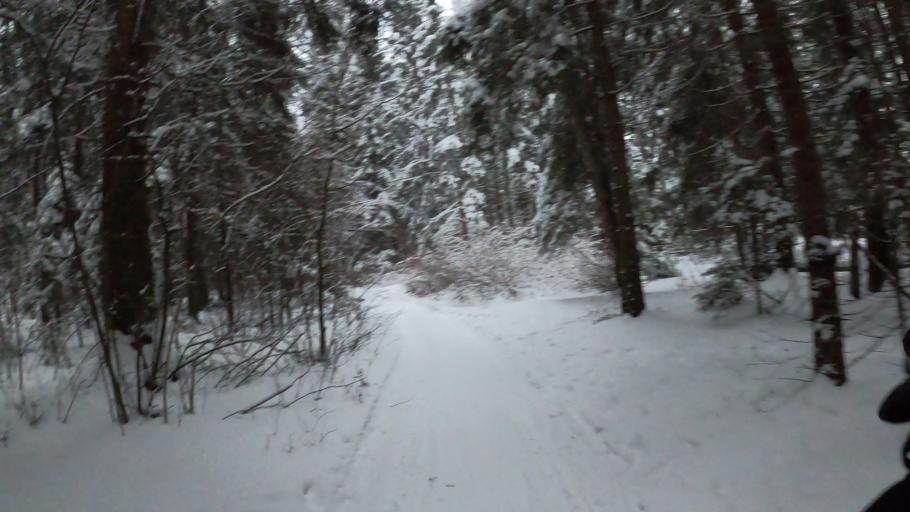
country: RU
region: Moskovskaya
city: Firsanovka
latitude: 55.9069
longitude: 37.2038
